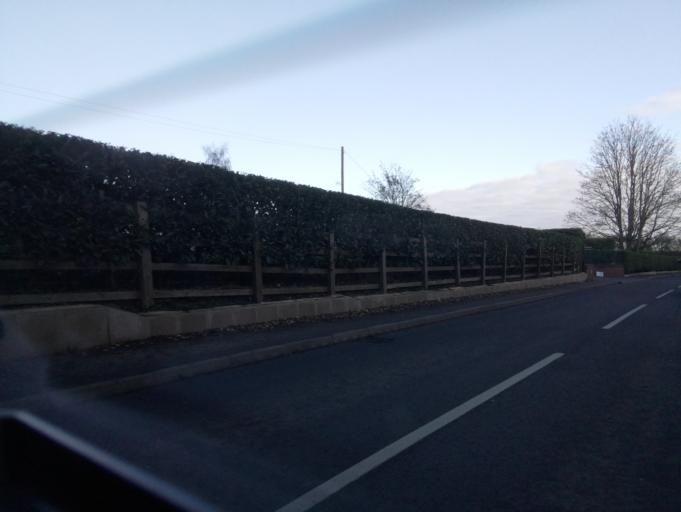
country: GB
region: England
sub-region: Staffordshire
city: Barton under Needwood
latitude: 52.7913
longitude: -1.6949
